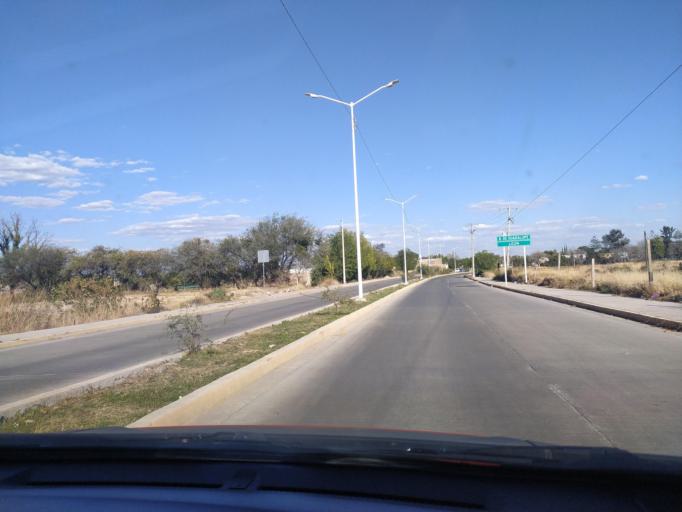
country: LA
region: Oudomxai
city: Muang La
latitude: 21.0178
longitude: 101.8347
